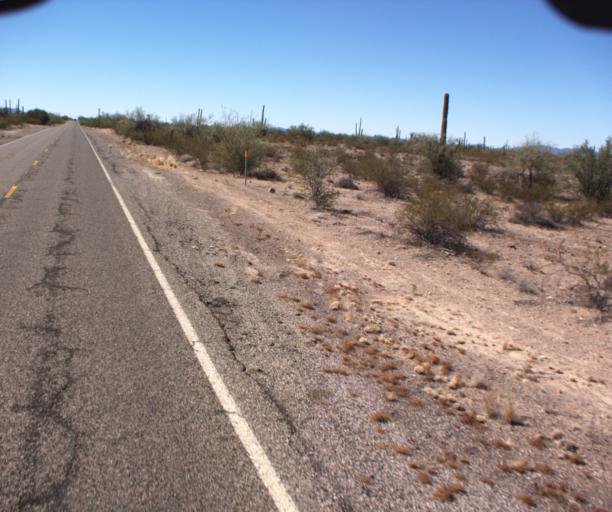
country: US
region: Arizona
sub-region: Pima County
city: Ajo
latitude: 32.2142
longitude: -112.7578
